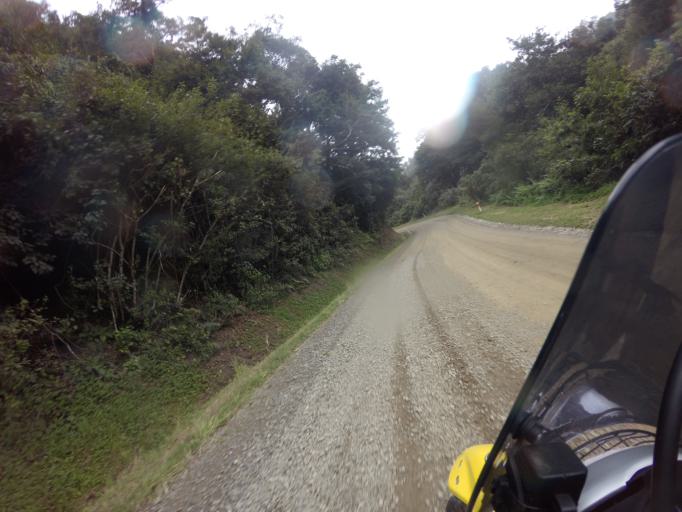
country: NZ
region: Bay of Plenty
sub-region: Whakatane District
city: Murupara
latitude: -38.6730
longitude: 177.0460
